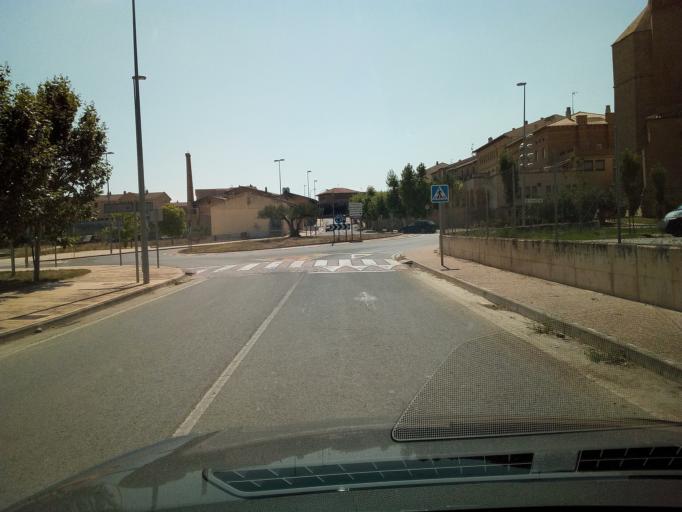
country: ES
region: Navarre
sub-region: Provincia de Navarra
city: Olite
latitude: 42.4801
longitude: -1.6472
